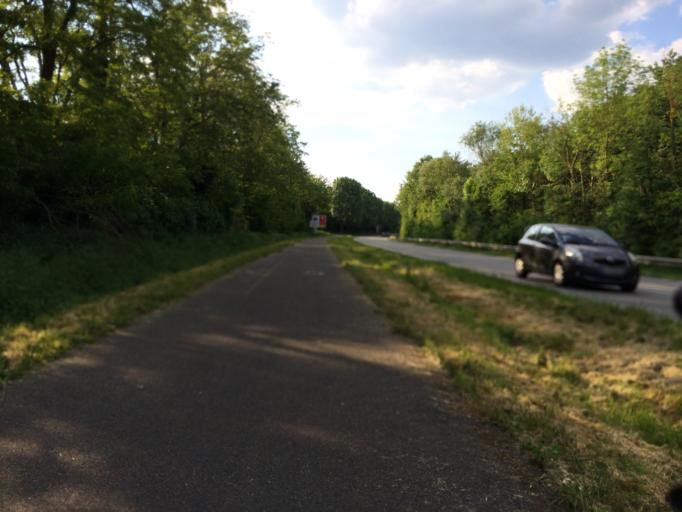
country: FR
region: Ile-de-France
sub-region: Departement de l'Essonne
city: Lisses
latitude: 48.6053
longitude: 2.4273
